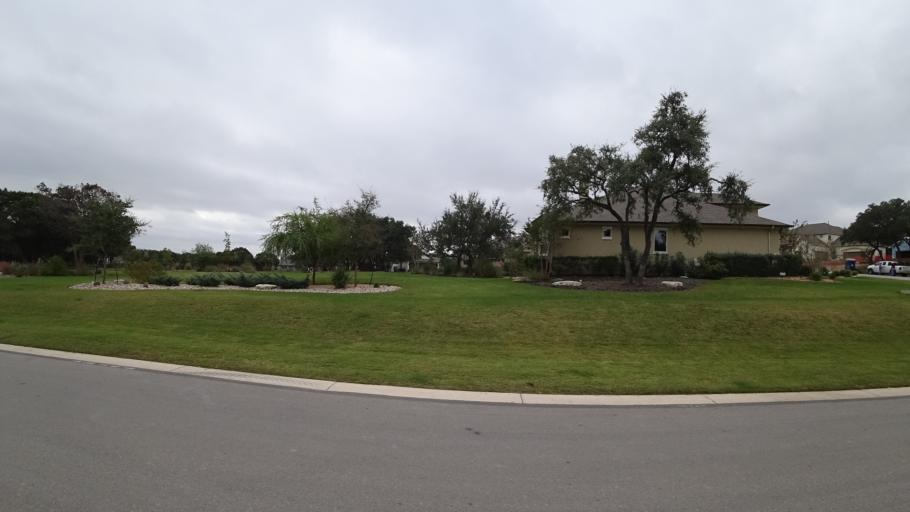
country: US
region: Texas
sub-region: Travis County
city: Barton Creek
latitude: 30.2569
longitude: -97.9133
